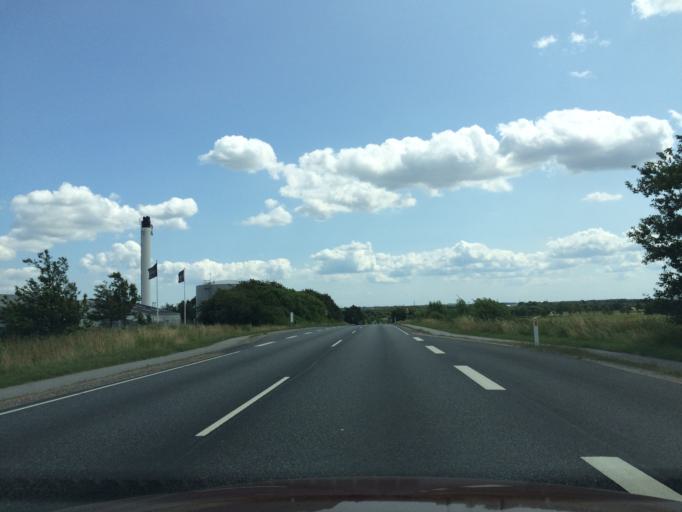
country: DK
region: Central Jutland
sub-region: Arhus Kommune
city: Sabro
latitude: 56.2061
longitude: 10.0418
